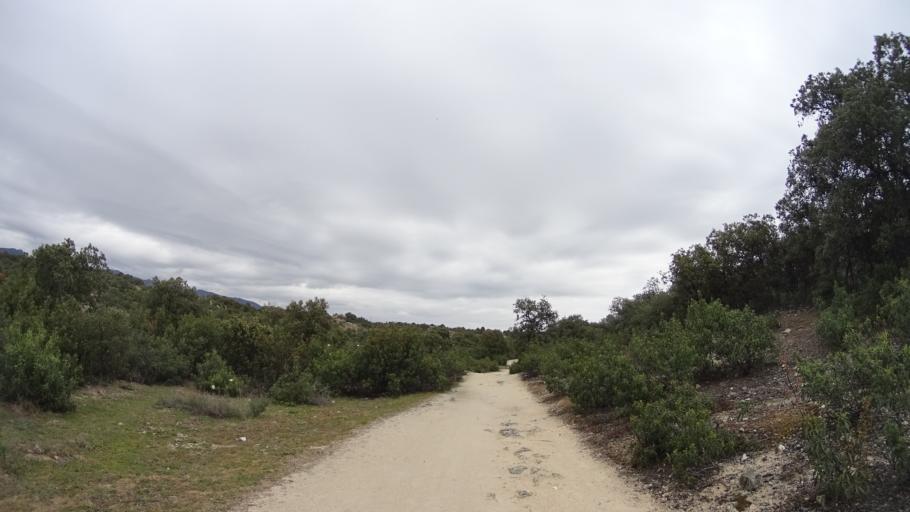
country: ES
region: Madrid
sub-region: Provincia de Madrid
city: Hoyo de Manzanares
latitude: 40.5966
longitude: -3.8857
